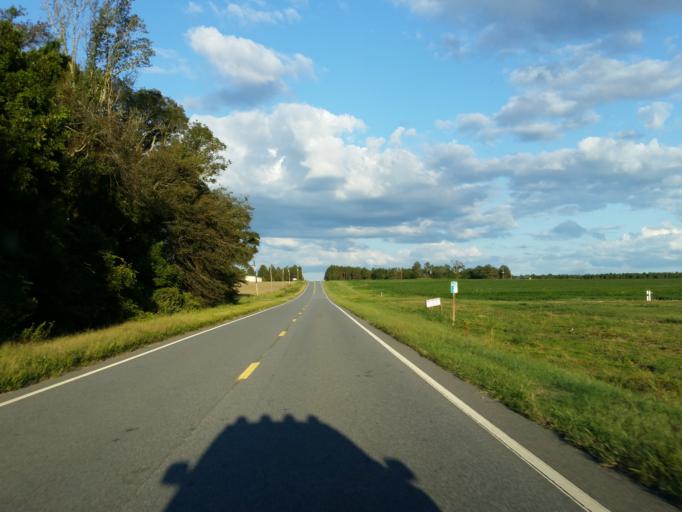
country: US
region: Georgia
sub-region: Dooly County
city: Vienna
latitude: 32.0863
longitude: -83.7345
